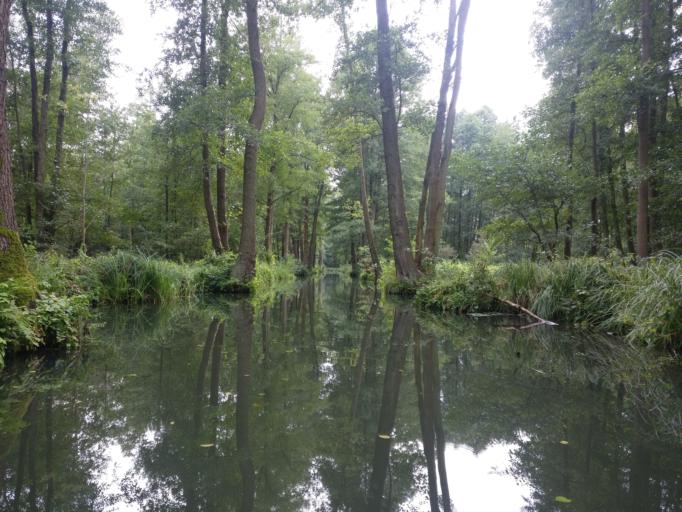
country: DE
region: Brandenburg
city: Lubbenau
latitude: 51.8614
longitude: 14.0362
